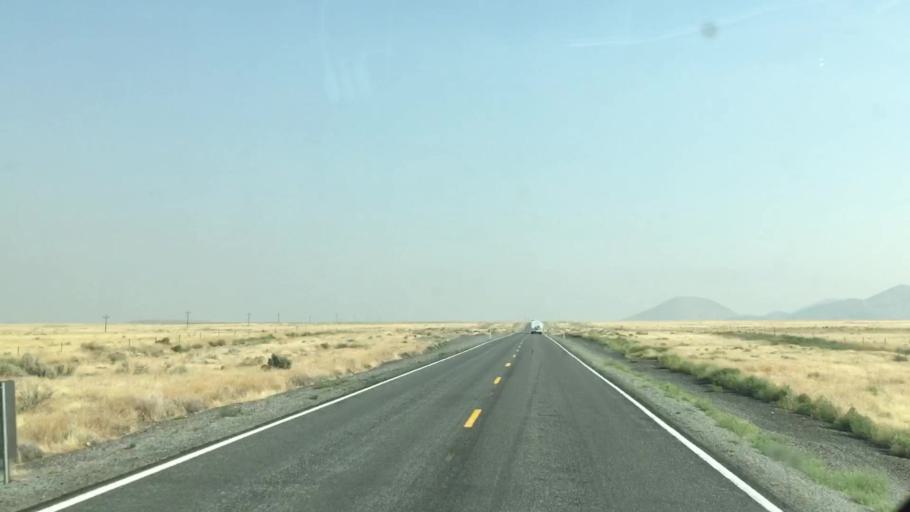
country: US
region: Nevada
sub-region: Lyon County
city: Fernley
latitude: 40.4701
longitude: -119.3343
